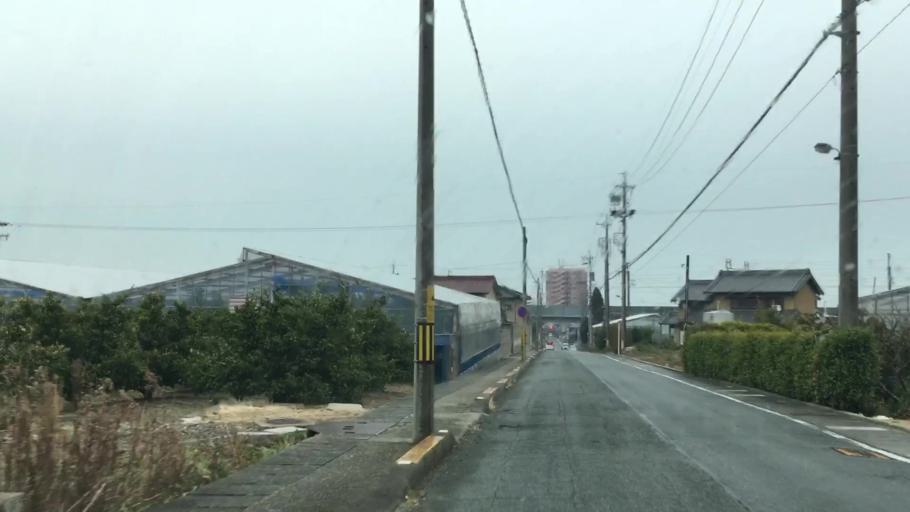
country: JP
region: Aichi
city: Gamagori
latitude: 34.8374
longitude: 137.2234
